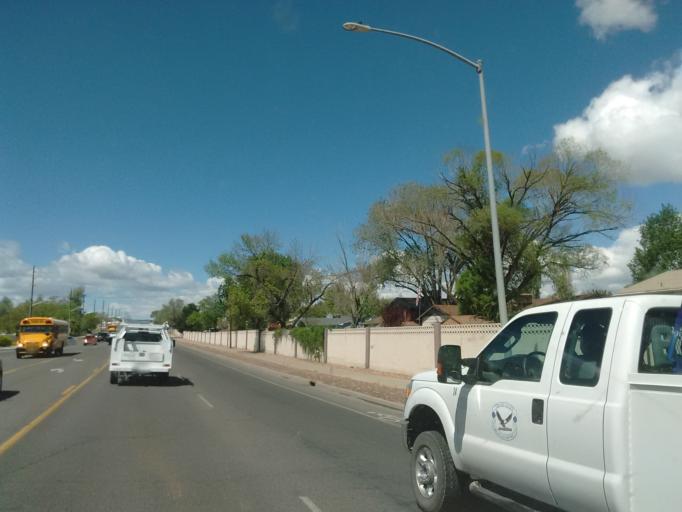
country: US
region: Colorado
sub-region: Mesa County
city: Fruitvale
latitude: 39.0919
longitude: -108.5168
